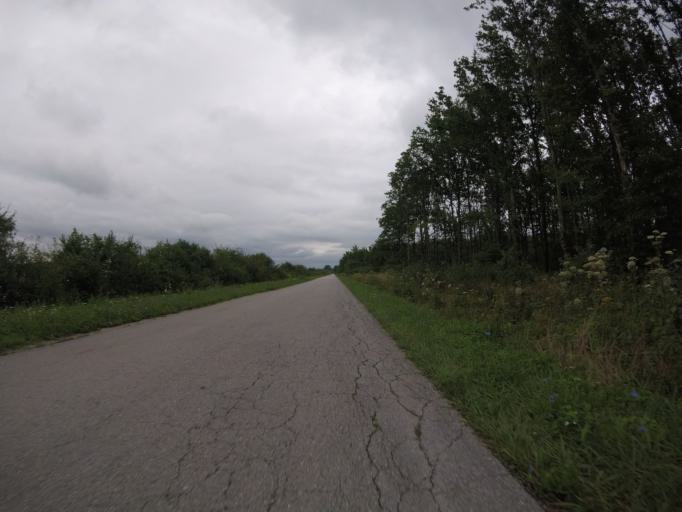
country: HR
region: Zagrebacka
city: Turopolje
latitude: 45.6422
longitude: 16.1304
